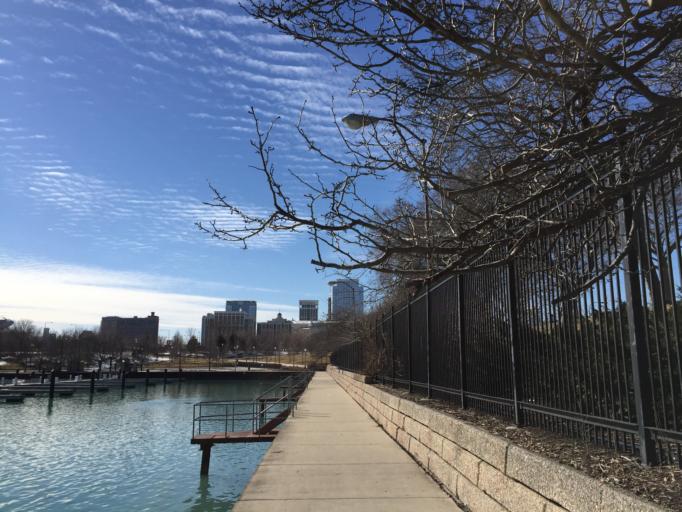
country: US
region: Illinois
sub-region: Cook County
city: Chicago
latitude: 41.8659
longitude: -87.6109
